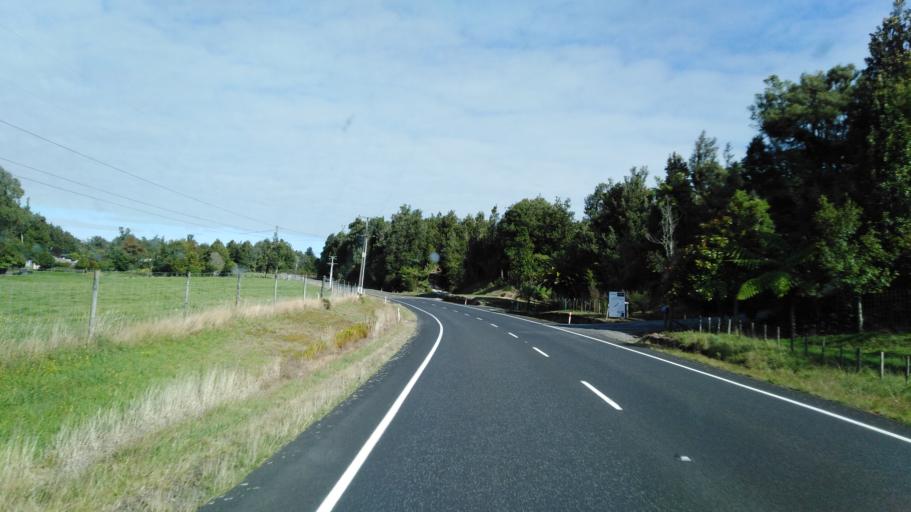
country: NZ
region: Bay of Plenty
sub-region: Tauranga City
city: Tauranga
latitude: -37.8703
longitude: 176.1407
